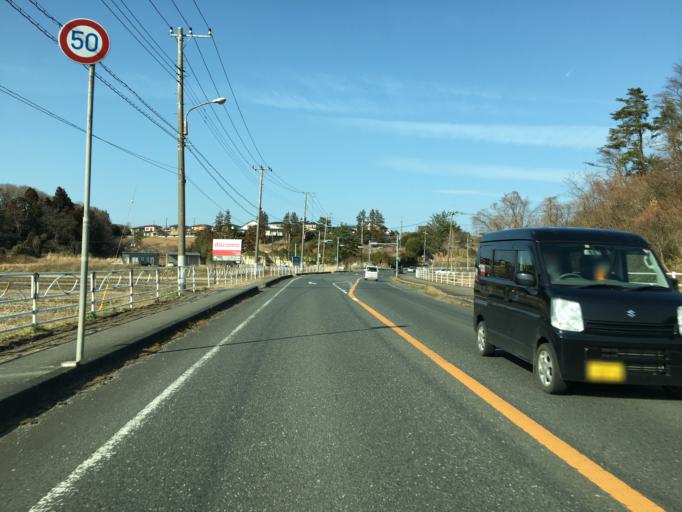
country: JP
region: Ibaraki
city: Kitaibaraki
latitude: 36.7628
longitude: 140.7280
